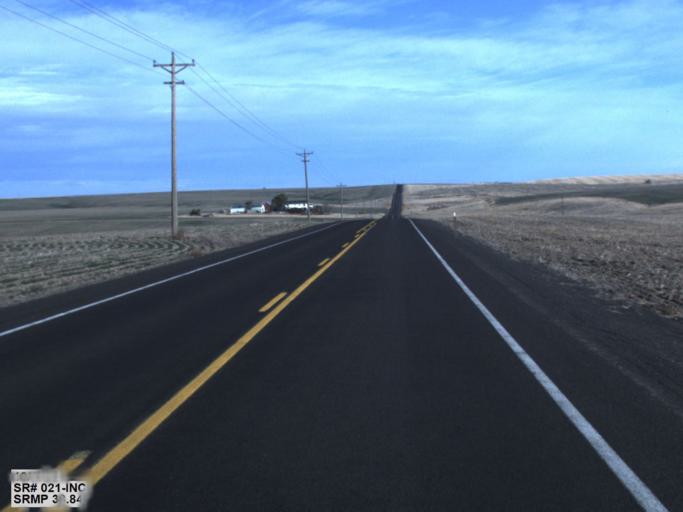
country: US
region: Washington
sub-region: Adams County
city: Ritzville
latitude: 47.1118
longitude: -118.6653
